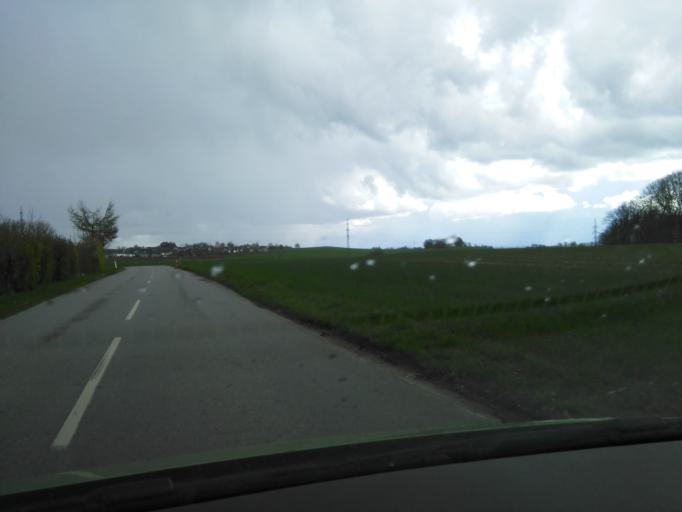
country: DK
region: Central Jutland
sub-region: Arhus Kommune
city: Trige
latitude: 56.2333
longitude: 10.1832
